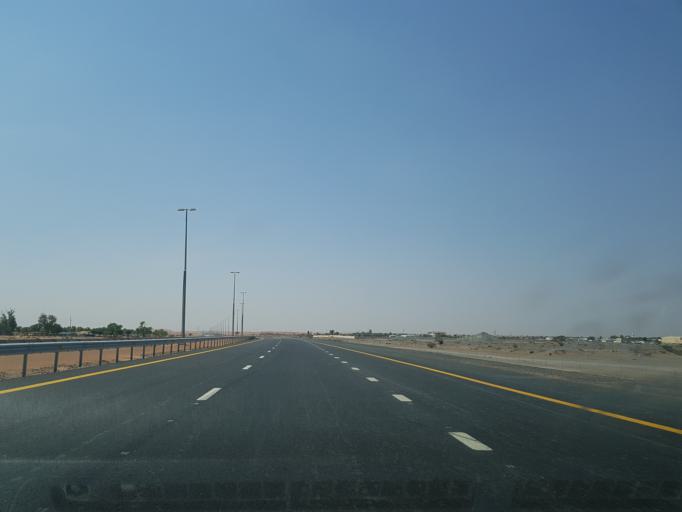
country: AE
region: Ash Shariqah
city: Adh Dhayd
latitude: 25.2351
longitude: 55.9057
